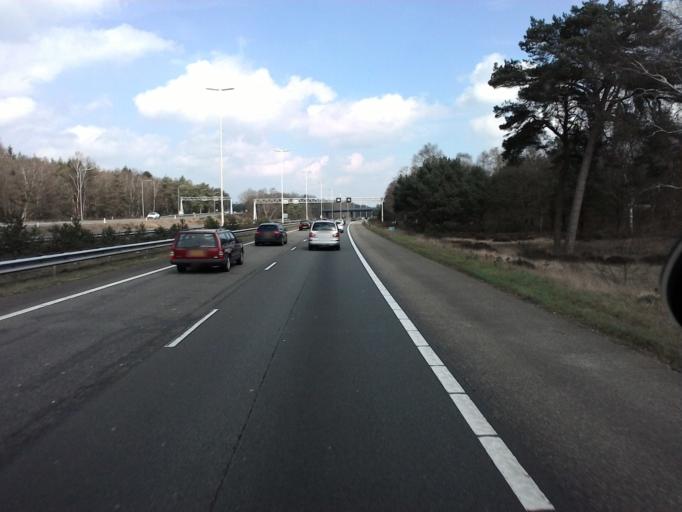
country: NL
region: North Holland
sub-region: Gemeente Hilversum
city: Hilversum
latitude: 52.1955
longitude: 5.1881
